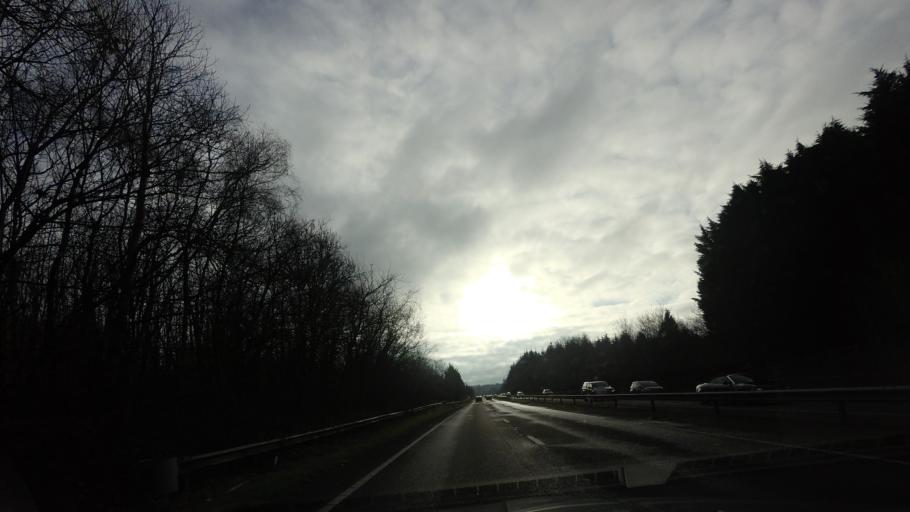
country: GB
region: England
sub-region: Kent
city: Sevenoaks
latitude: 51.2632
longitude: 0.1710
